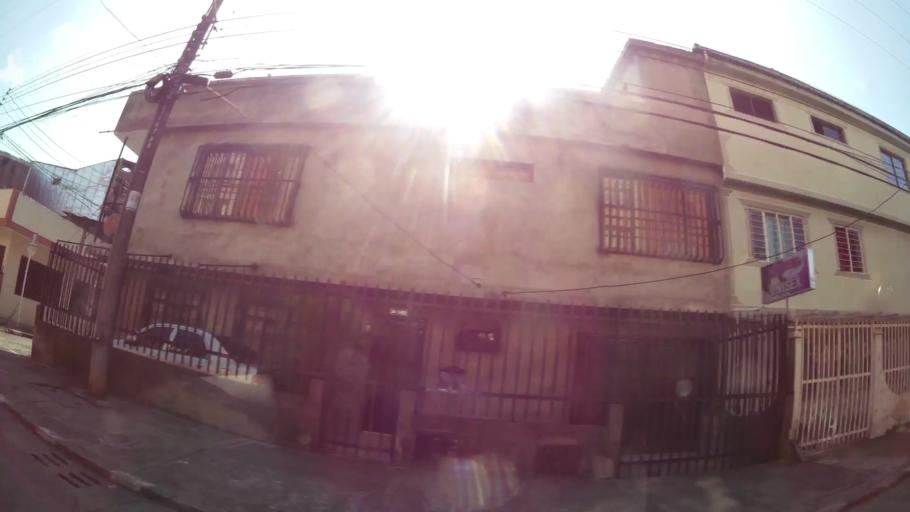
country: CO
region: Valle del Cauca
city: Cali
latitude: 3.4100
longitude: -76.5268
